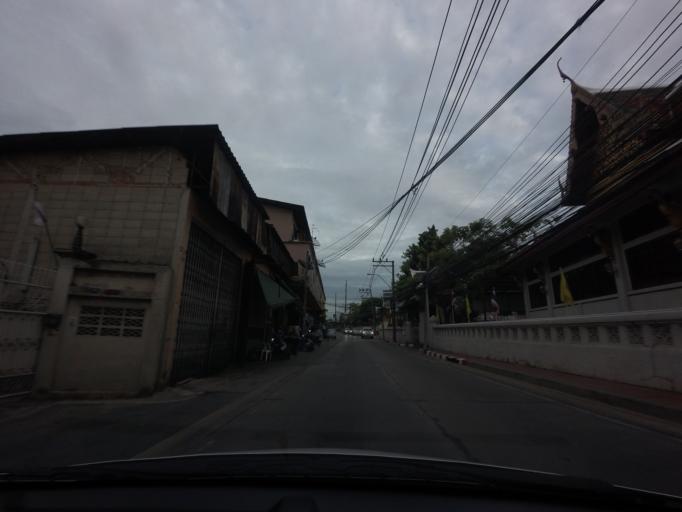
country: TH
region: Bangkok
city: Chom Thong
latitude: 13.6800
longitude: 100.4644
